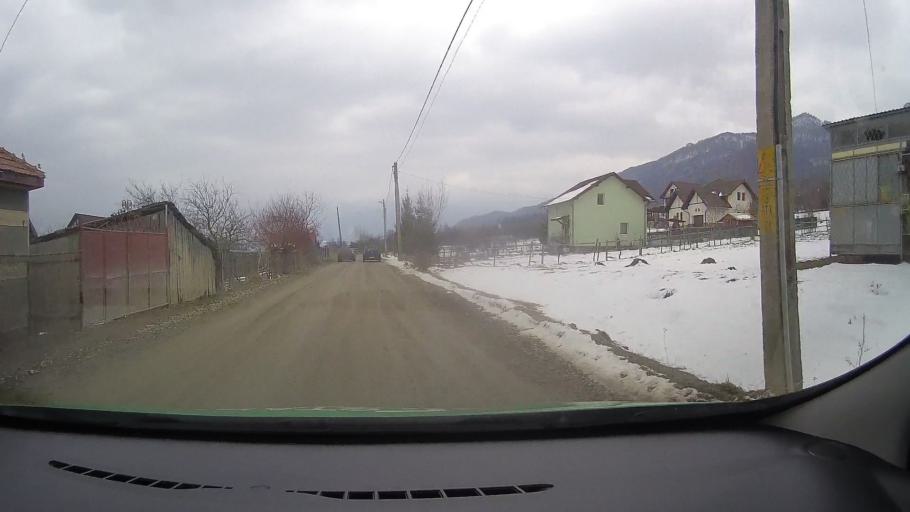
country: RO
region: Brasov
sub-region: Comuna Zarnesti
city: Zarnesti
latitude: 45.5440
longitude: 25.3234
